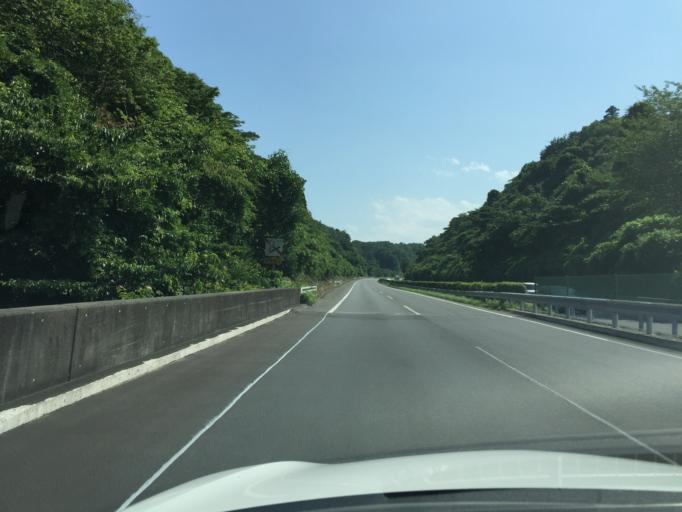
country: JP
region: Fukushima
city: Iwaki
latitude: 36.9780
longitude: 140.7952
